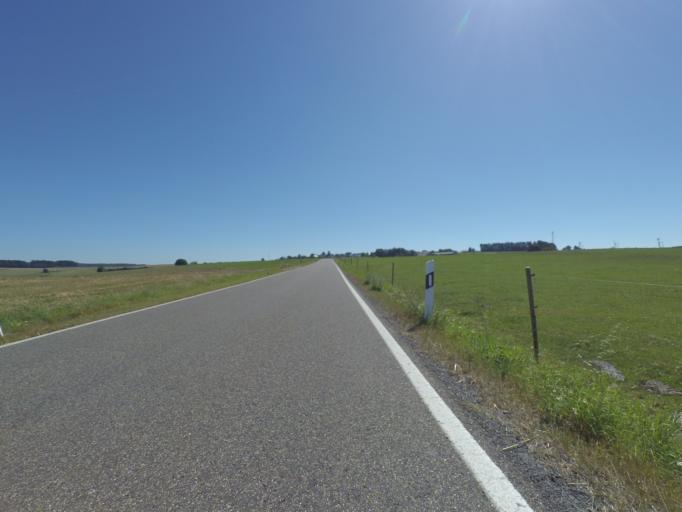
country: DE
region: Rheinland-Pfalz
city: Lutzerath
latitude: 50.1382
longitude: 7.0100
